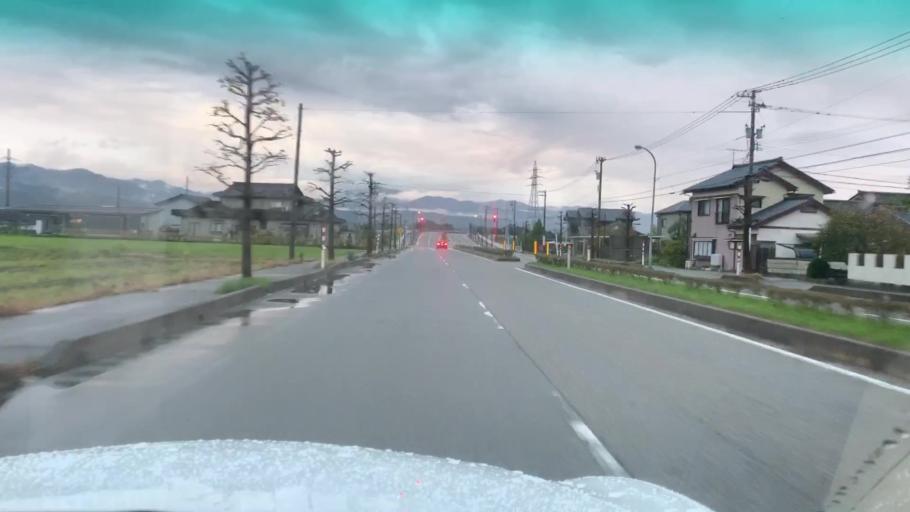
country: JP
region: Toyama
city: Kamiichi
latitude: 36.6975
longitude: 137.3427
